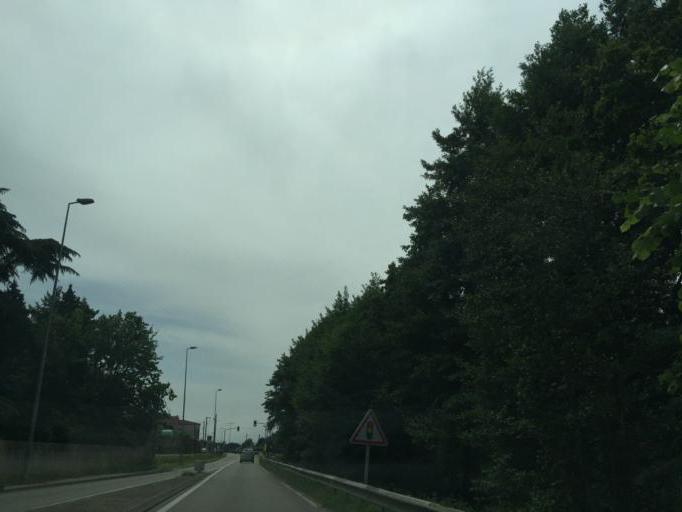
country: FR
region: Rhone-Alpes
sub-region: Departement de l'Ardeche
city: Saint-Marcel-les-Annonay
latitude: 45.2829
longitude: 4.6341
